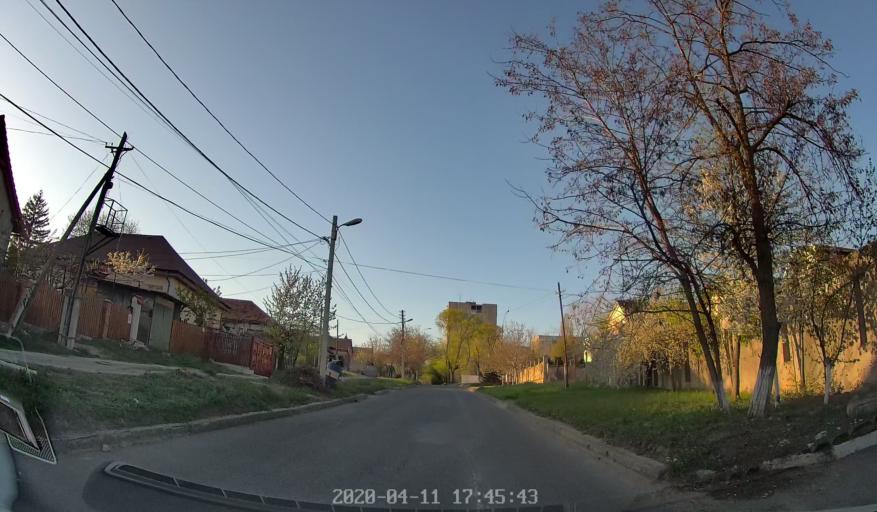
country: MD
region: Chisinau
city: Chisinau
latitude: 46.9872
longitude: 28.8221
